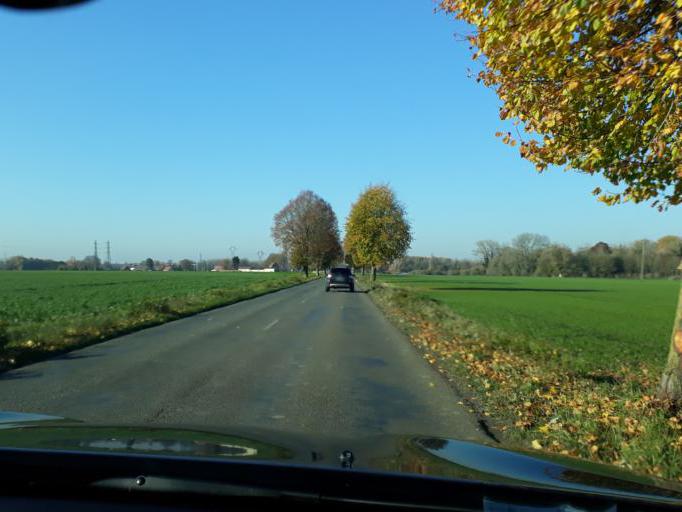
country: FR
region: Nord-Pas-de-Calais
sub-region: Departement du Nord
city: Guesnain
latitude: 50.3617
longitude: 3.1526
